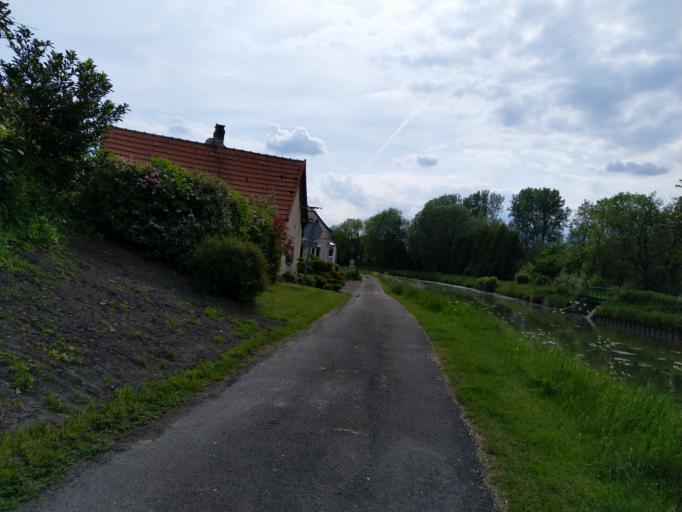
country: FR
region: Picardie
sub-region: Departement de l'Aisne
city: Etreux
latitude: 49.9702
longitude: 3.6265
